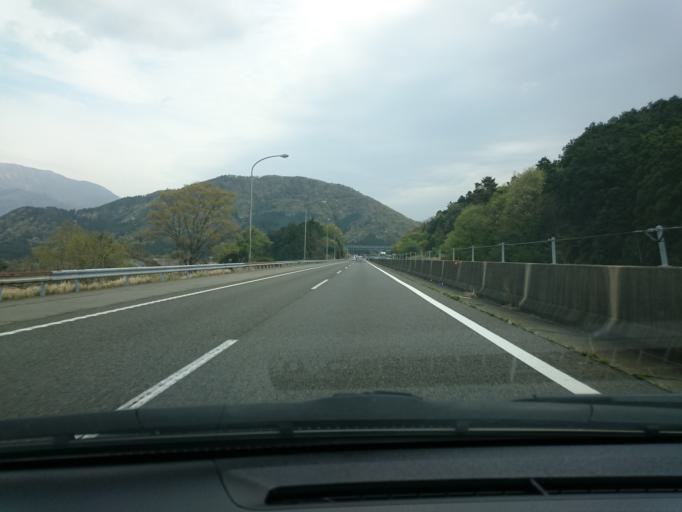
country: JP
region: Gifu
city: Tarui
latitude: 35.3403
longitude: 136.4063
